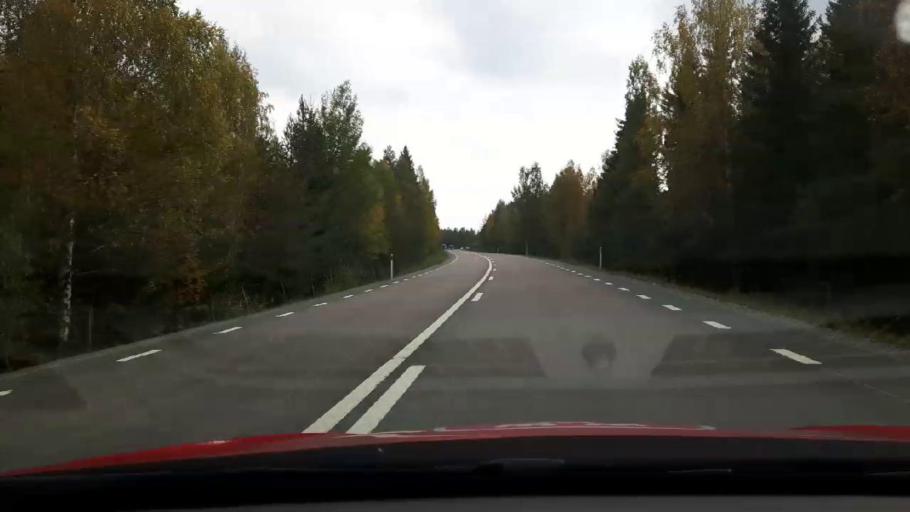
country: SE
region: Gaevleborg
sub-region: Bollnas Kommun
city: Kilafors
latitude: 61.2734
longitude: 16.5296
